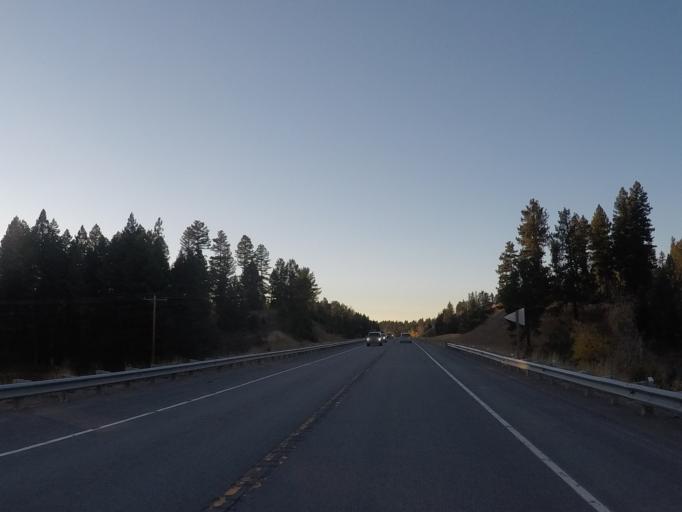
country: US
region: Montana
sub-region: Lewis and Clark County
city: Lincoln
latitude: 47.0107
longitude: -113.0619
